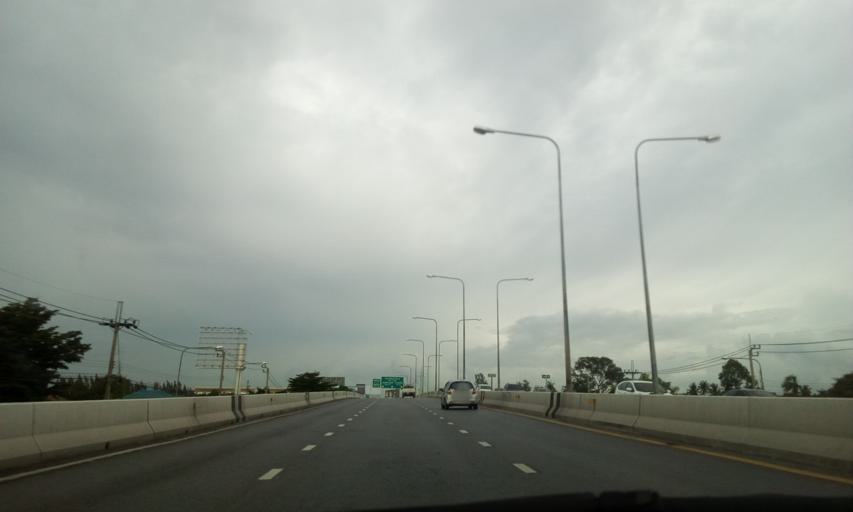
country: TH
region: Nonthaburi
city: Pak Kret
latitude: 13.9219
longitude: 100.4808
